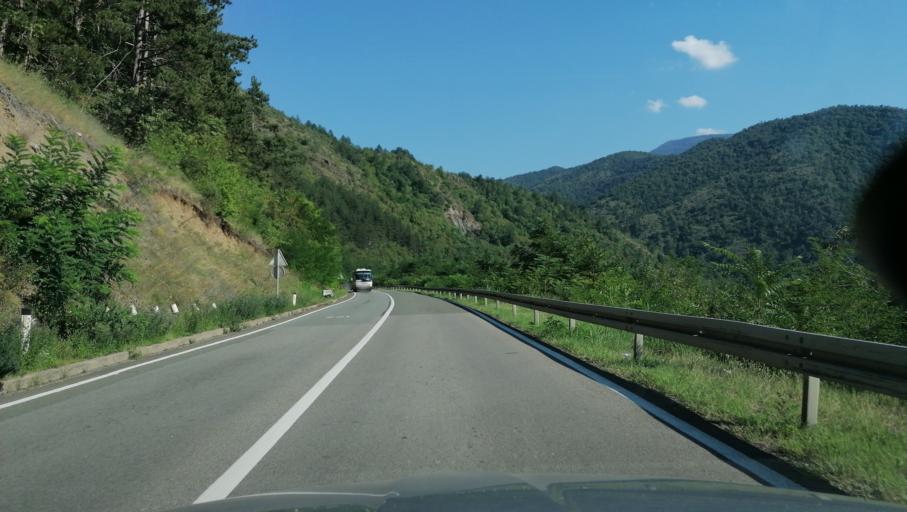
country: RS
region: Central Serbia
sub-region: Raski Okrug
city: Kraljevo
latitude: 43.6660
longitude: 20.5787
